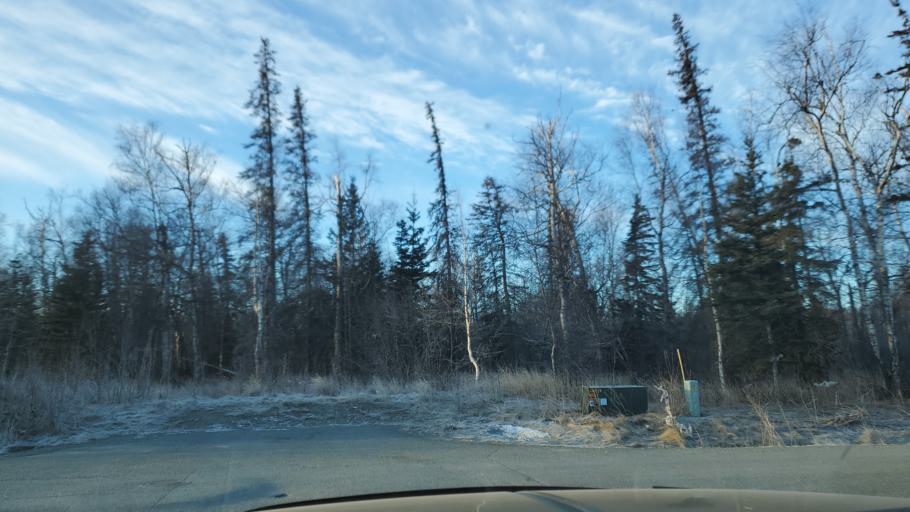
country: US
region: Alaska
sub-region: Matanuska-Susitna Borough
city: Wasilla
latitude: 61.5756
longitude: -149.4205
